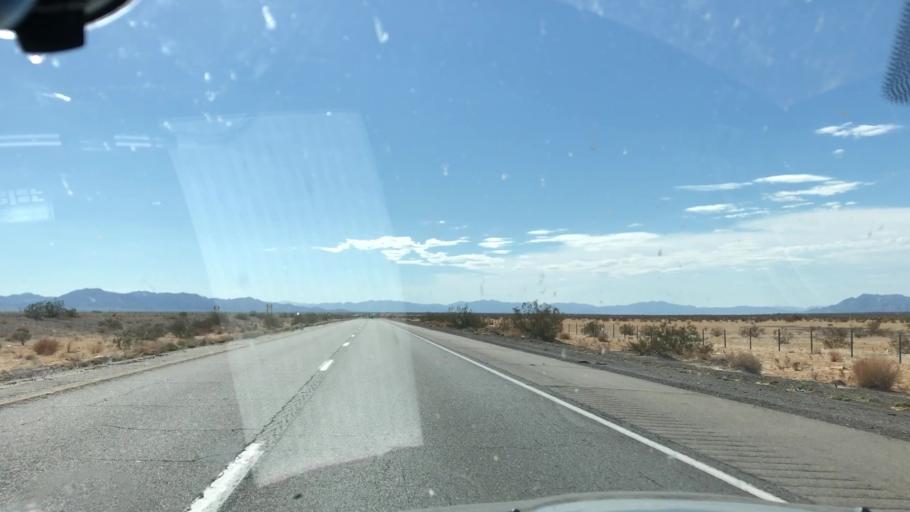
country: US
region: California
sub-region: Riverside County
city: Mesa Verde
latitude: 33.6377
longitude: -115.0877
